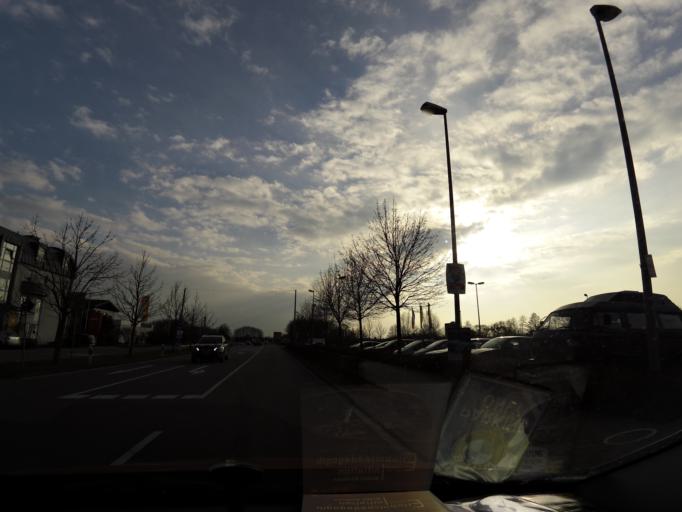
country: DE
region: Baden-Wuerttemberg
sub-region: Freiburg Region
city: Rheinau
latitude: 48.6631
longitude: 7.9386
